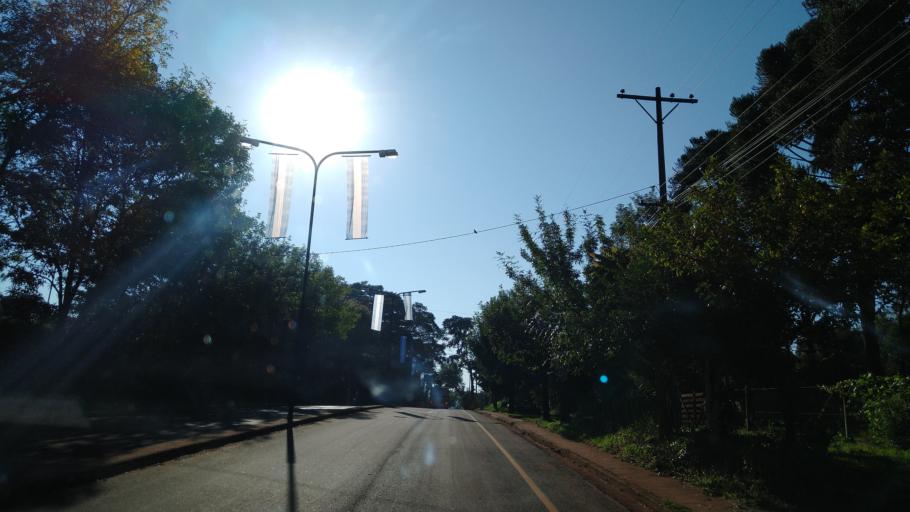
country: AR
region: Misiones
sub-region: Departamento de Montecarlo
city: Montecarlo
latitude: -26.5715
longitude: -54.7364
